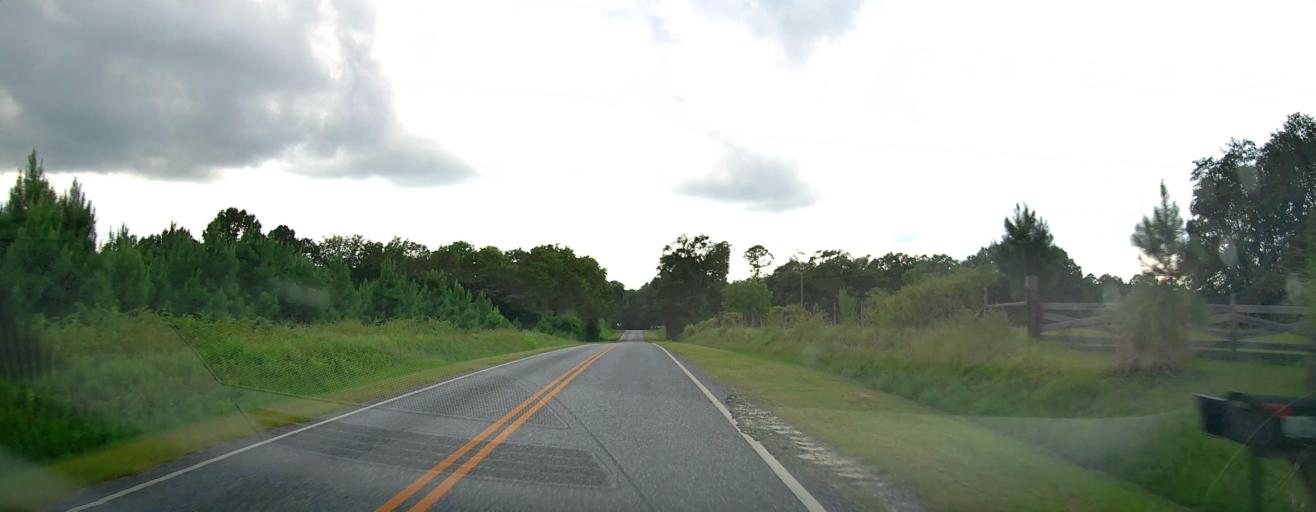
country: US
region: Georgia
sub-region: Crawford County
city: Roberta
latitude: 32.7031
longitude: -84.0134
